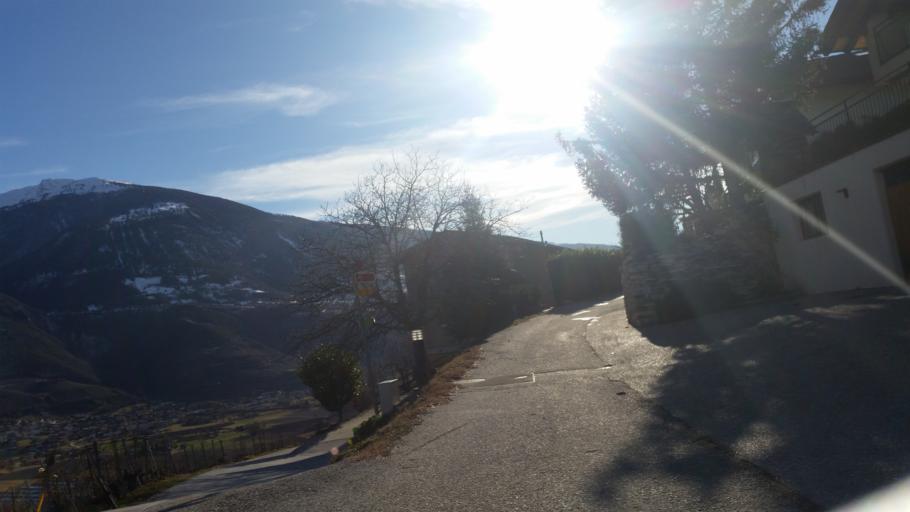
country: CH
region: Valais
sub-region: Sierre District
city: Chalais
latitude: 46.2825
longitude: 7.5000
